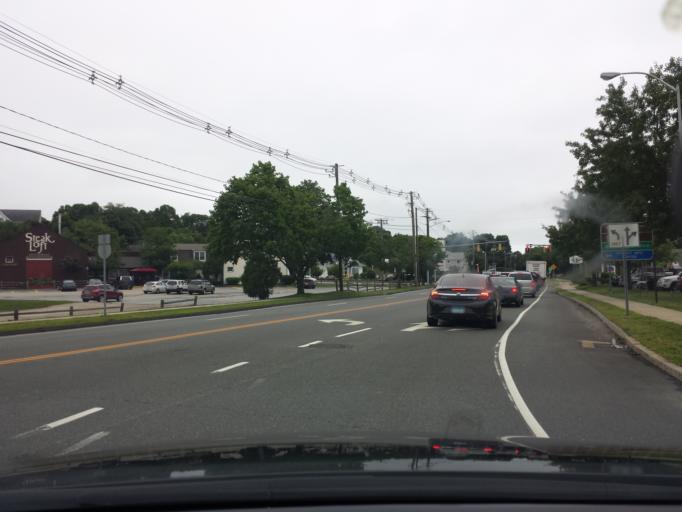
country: US
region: Connecticut
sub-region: New London County
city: Old Mystic
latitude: 41.3739
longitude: -71.9599
